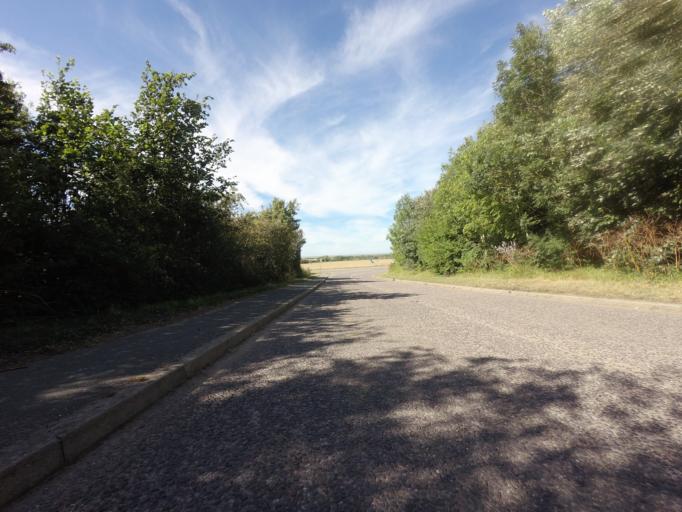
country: GB
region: England
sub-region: Kent
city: Birchington-on-Sea
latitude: 51.3602
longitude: 1.2448
